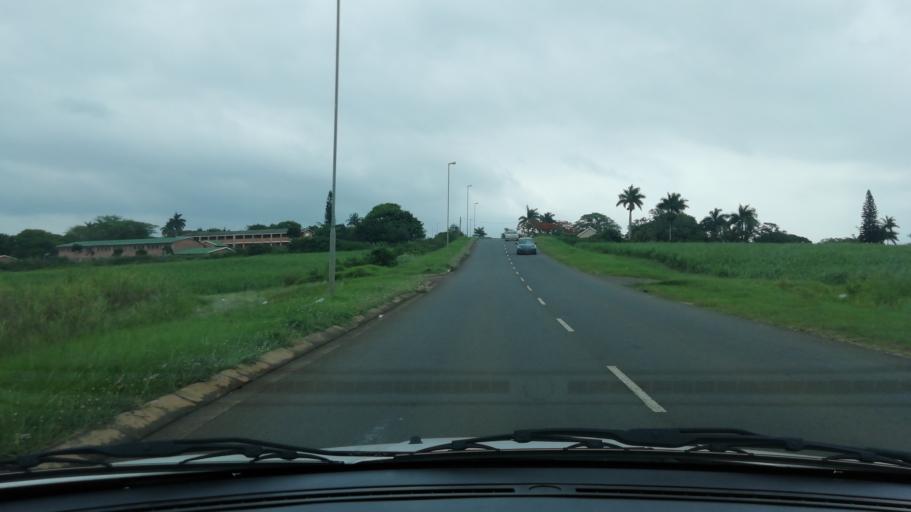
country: ZA
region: KwaZulu-Natal
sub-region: uThungulu District Municipality
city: Empangeni
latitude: -28.7394
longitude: 31.9049
